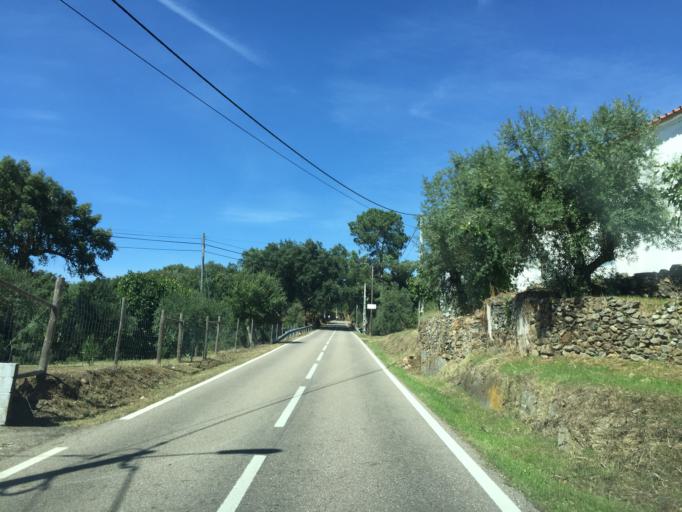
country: PT
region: Portalegre
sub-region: Marvao
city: Marvao
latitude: 39.3920
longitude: -7.3887
